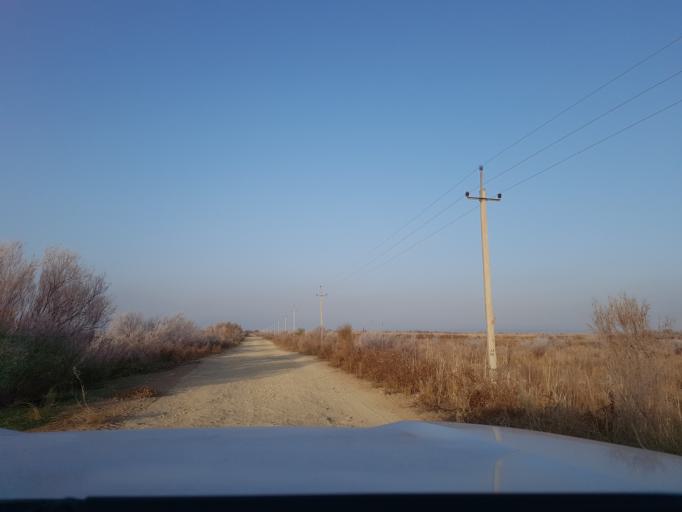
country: TM
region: Dasoguz
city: Koeneuergench
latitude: 41.8504
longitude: 58.3069
